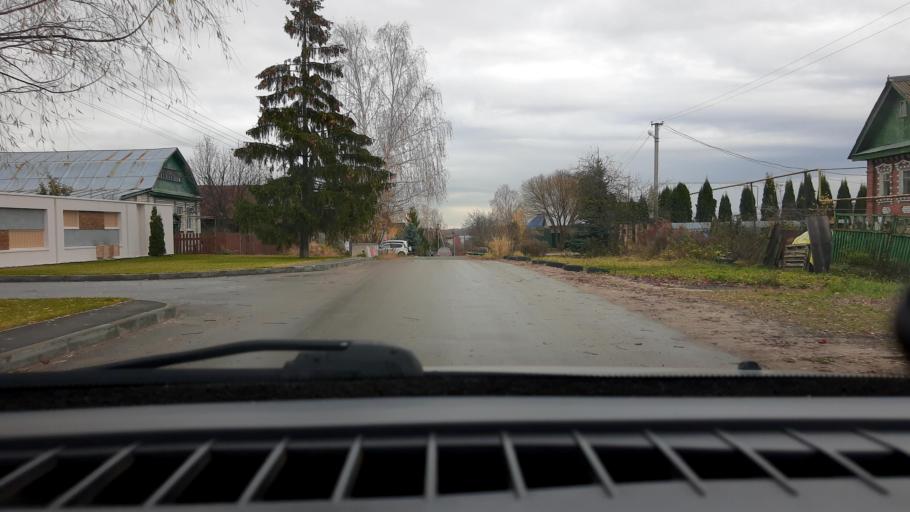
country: RU
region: Nizjnij Novgorod
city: Afonino
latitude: 56.1916
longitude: 44.0851
